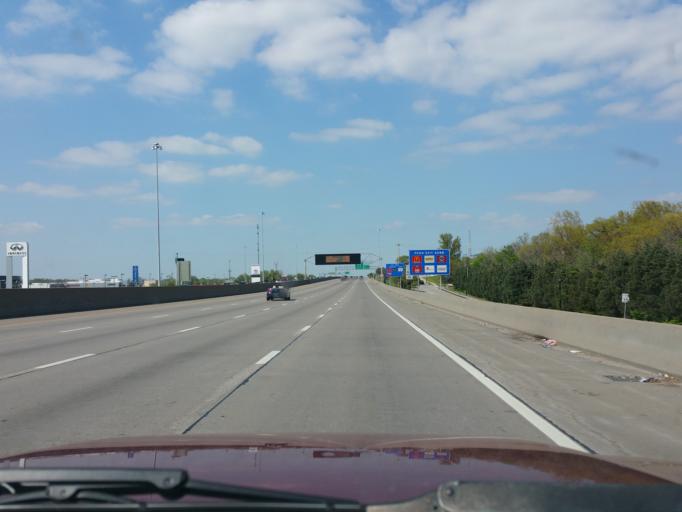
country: US
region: Kansas
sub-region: Johnson County
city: Merriam
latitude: 39.0017
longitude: -94.6944
